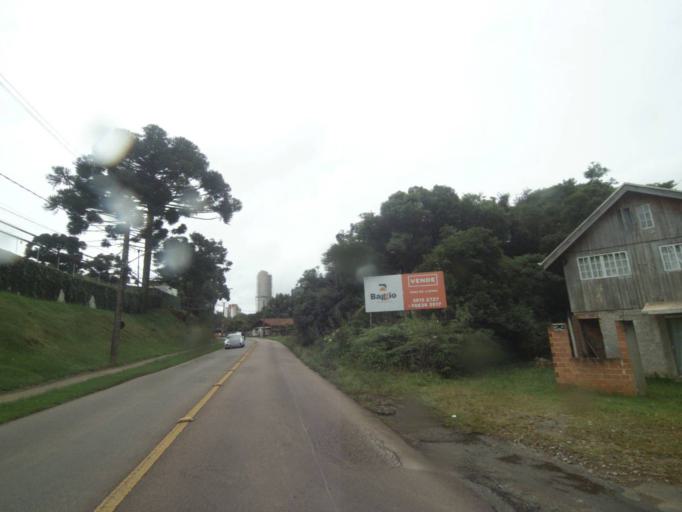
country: BR
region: Parana
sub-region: Curitiba
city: Curitiba
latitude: -25.4471
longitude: -49.3352
